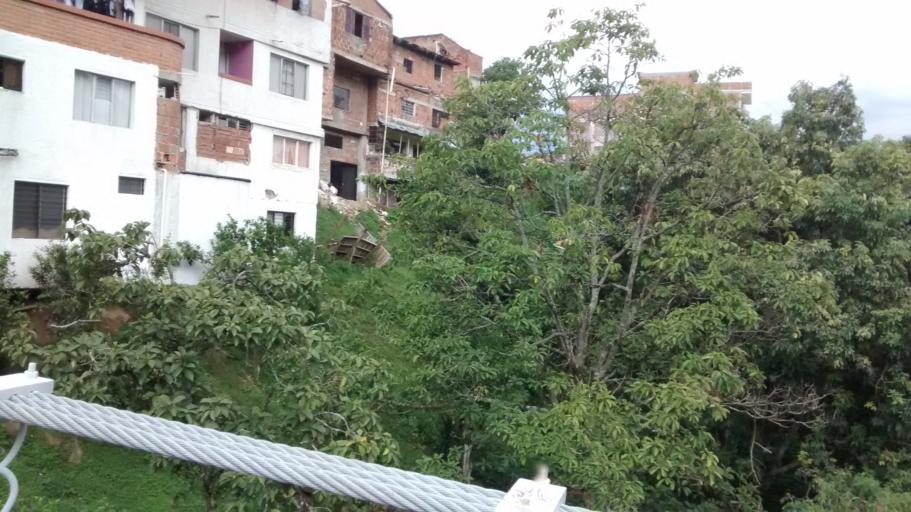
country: CO
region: Antioquia
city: Medellin
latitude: 6.2769
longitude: -75.6360
